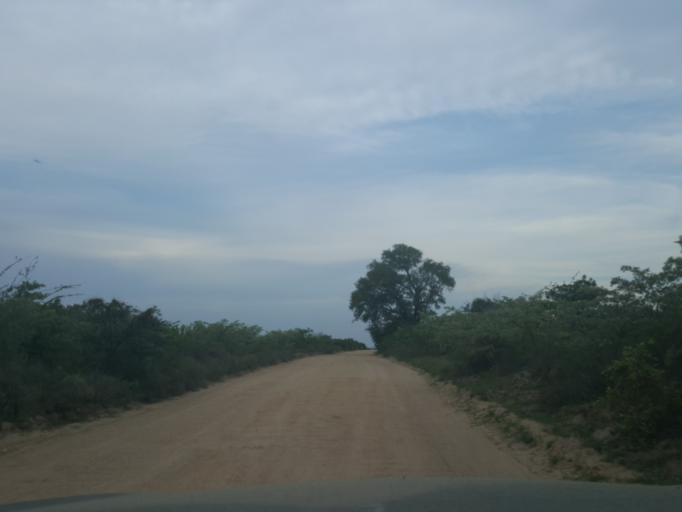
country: ZA
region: Limpopo
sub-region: Mopani District Municipality
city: Hoedspruit
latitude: -24.5850
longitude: 30.9786
